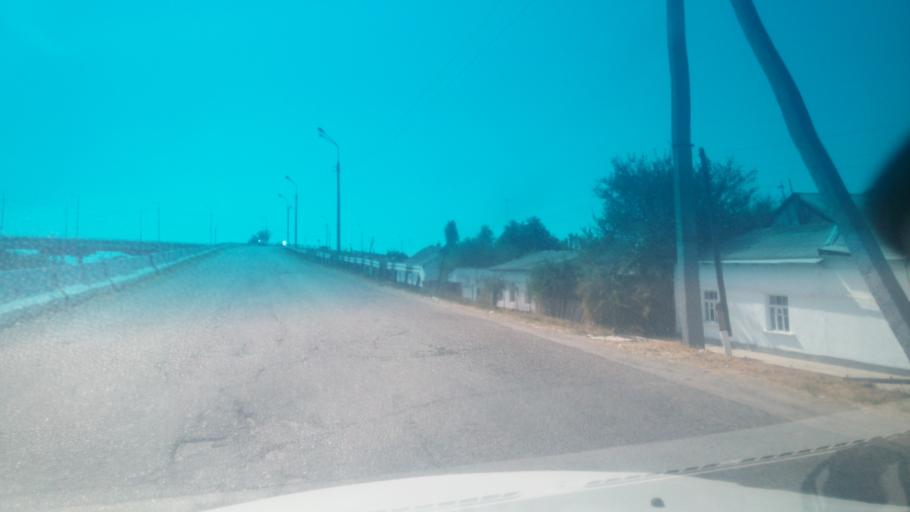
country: UZ
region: Sirdaryo
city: Sirdaryo
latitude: 40.8055
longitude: 68.6763
